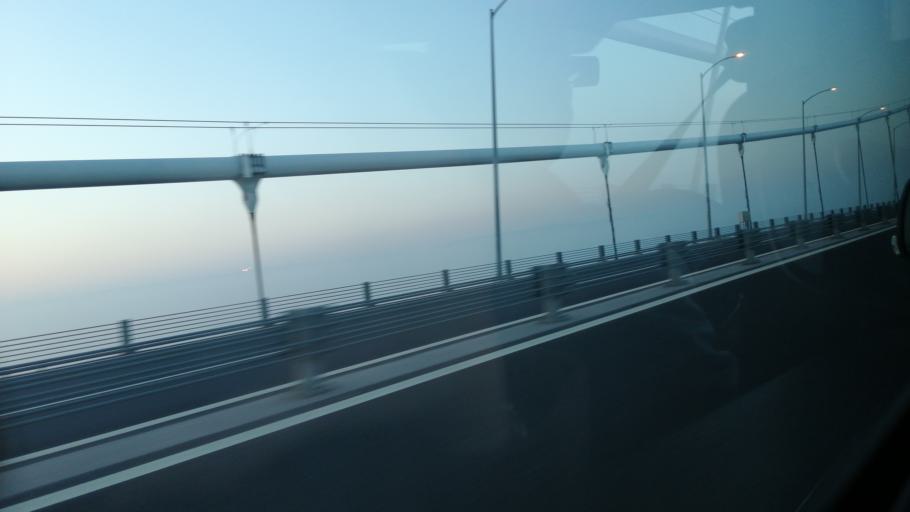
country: TR
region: Kocaeli
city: Tavsancil
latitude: 40.7554
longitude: 29.5160
